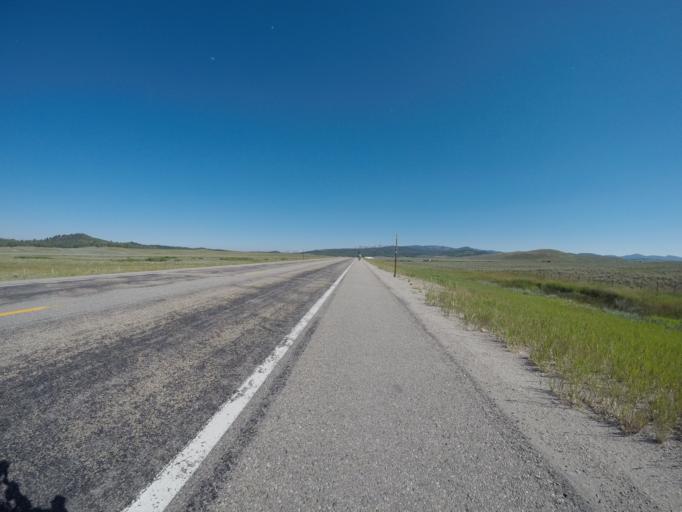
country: US
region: Wyoming
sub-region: Sublette County
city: Pinedale
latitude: 43.1087
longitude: -110.1726
